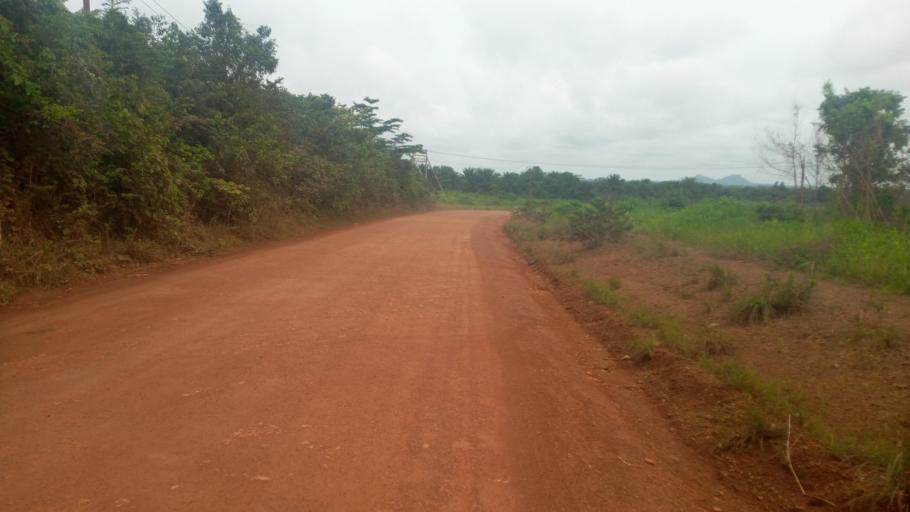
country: SL
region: Southern Province
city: Mogbwemo
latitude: 7.7408
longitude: -12.2877
